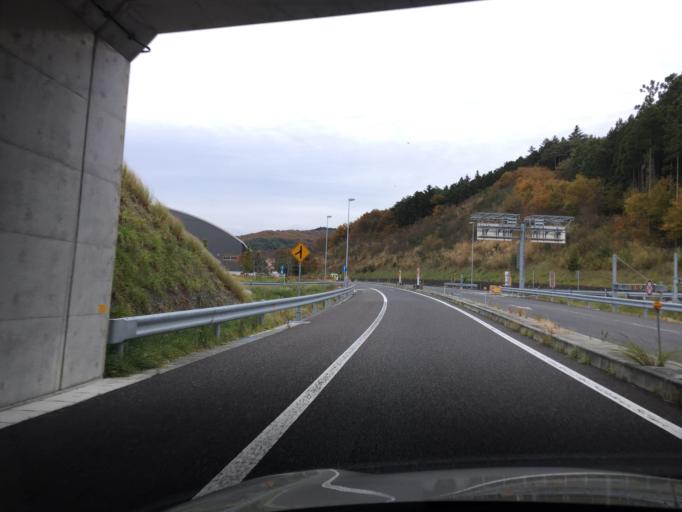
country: JP
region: Fukushima
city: Ishikawa
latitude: 37.2474
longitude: 140.5598
